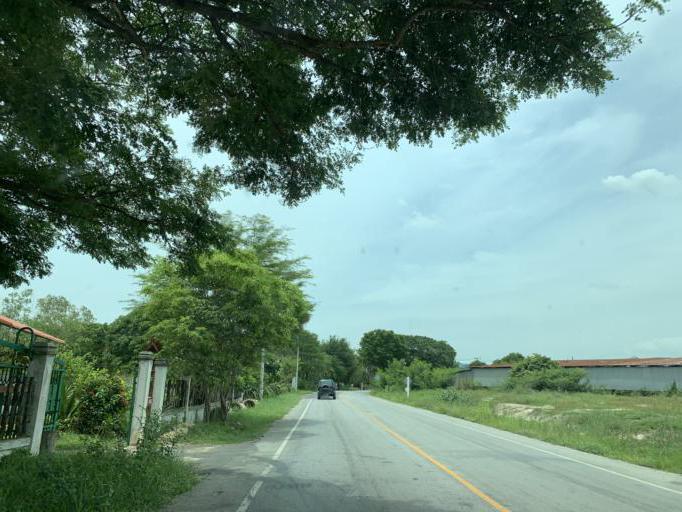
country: TH
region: Uthai Thani
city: Uthai Thani
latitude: 15.4032
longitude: 100.0269
